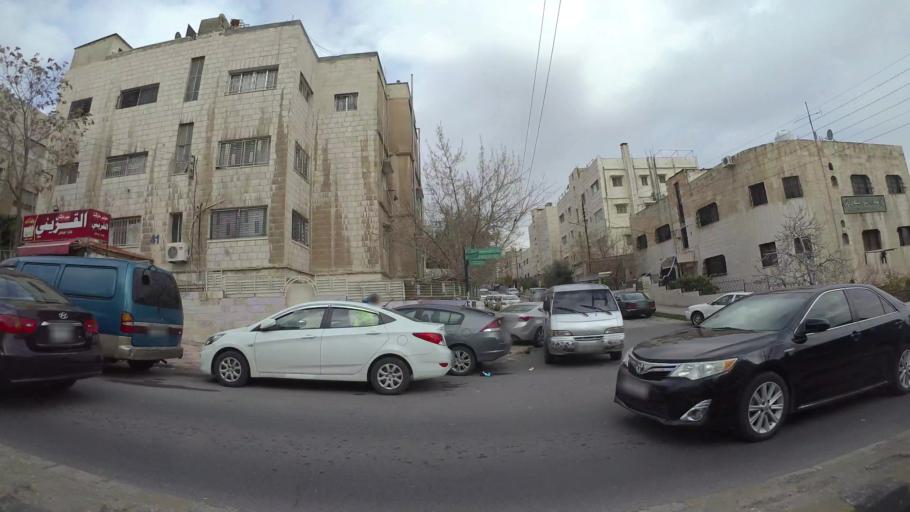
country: JO
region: Amman
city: Amman
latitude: 31.9716
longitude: 35.9219
